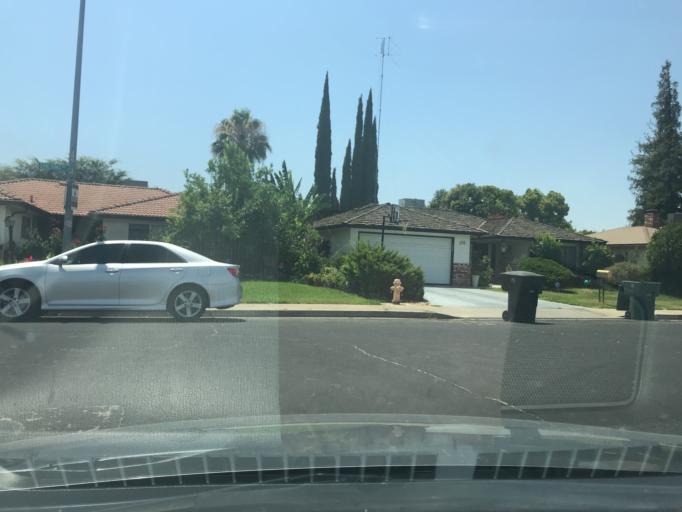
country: US
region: California
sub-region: Merced County
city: Atwater
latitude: 37.3618
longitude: -120.6093
